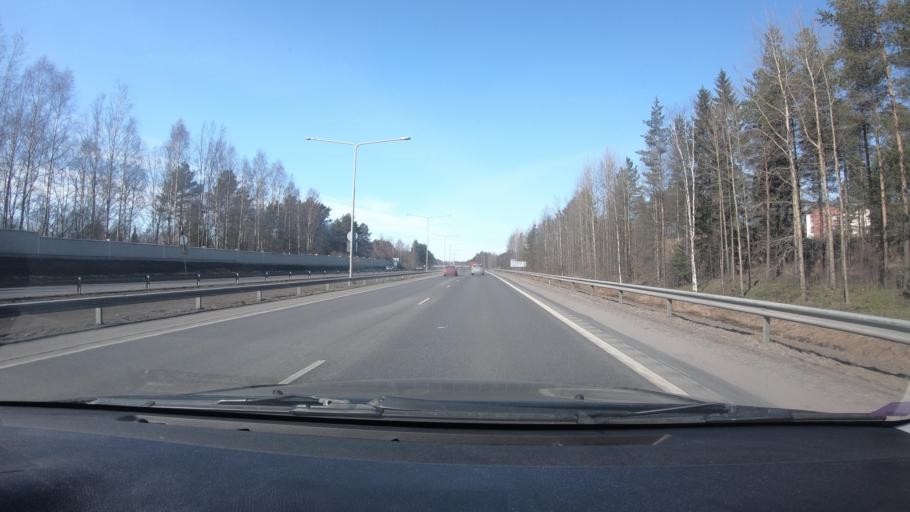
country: FI
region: Northern Ostrobothnia
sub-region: Oulu
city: Oulu
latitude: 65.0367
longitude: 25.4847
